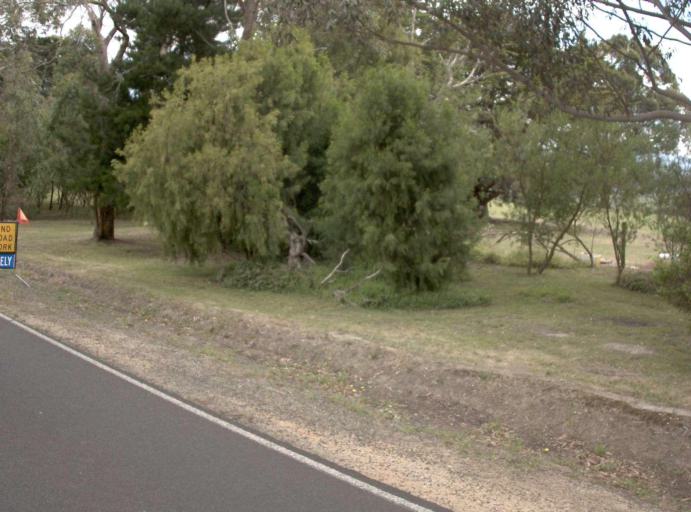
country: AU
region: Victoria
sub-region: Latrobe
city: Moe
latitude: -38.1092
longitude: 146.2477
